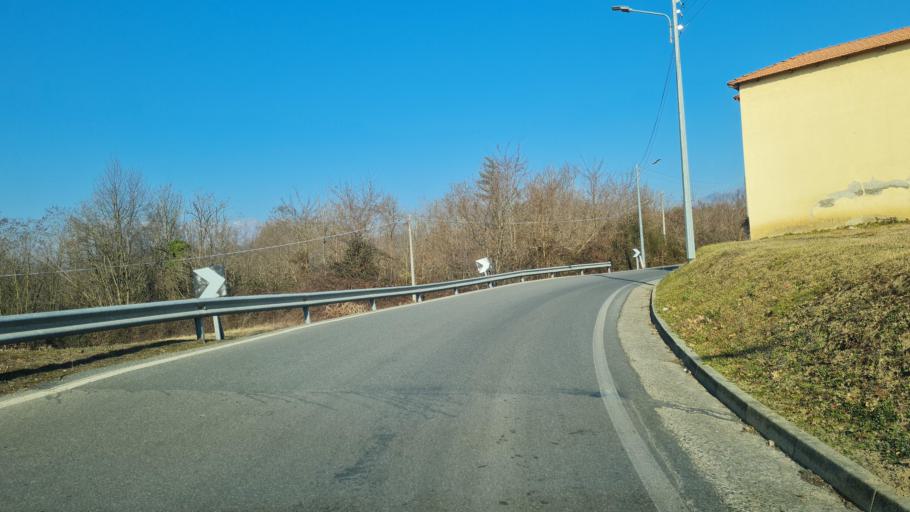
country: IT
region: Piedmont
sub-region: Provincia di Biella
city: Piatto
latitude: 45.5845
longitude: 8.1370
